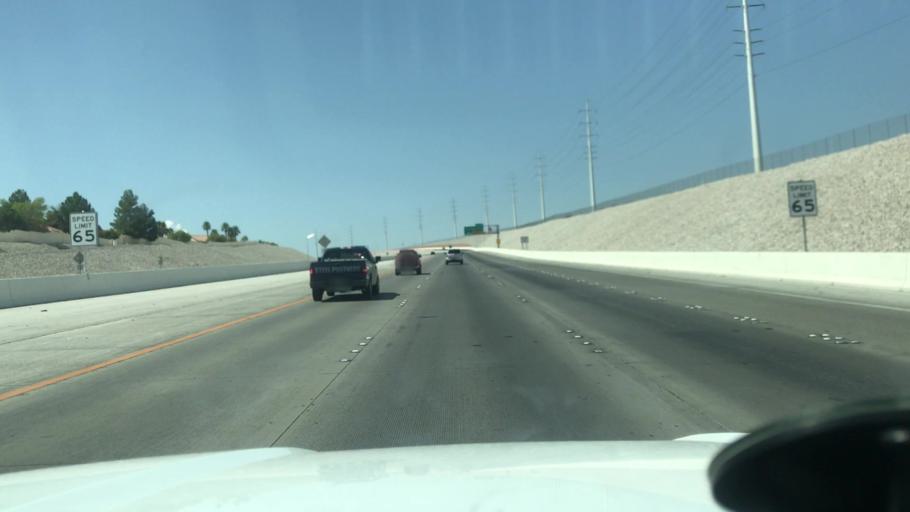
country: US
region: Nevada
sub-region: Clark County
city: Summerlin South
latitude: 36.2129
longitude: -115.3344
